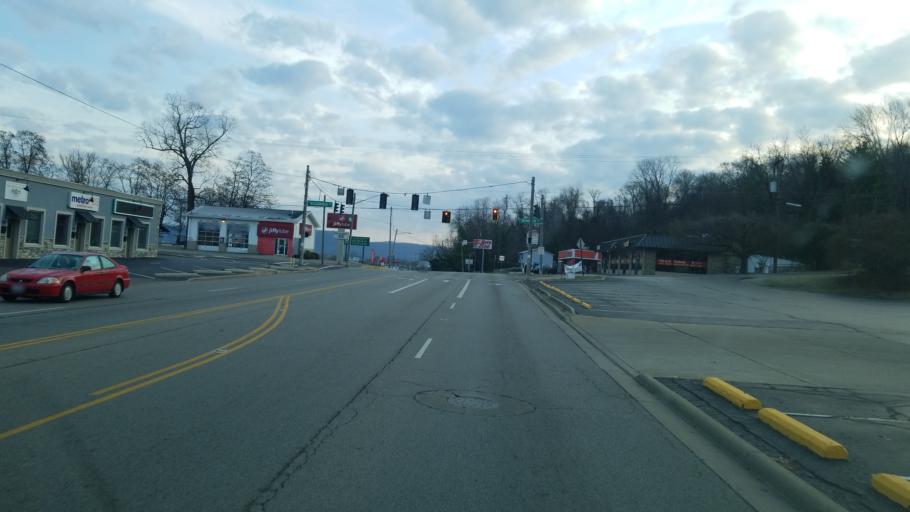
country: US
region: Ohio
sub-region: Ross County
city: Chillicothe
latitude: 39.3336
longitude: -83.0057
